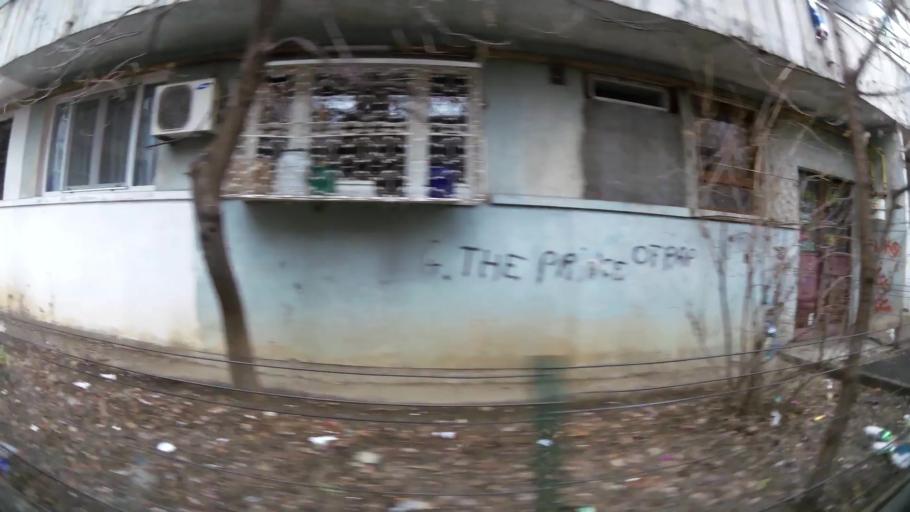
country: RO
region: Ilfov
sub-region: Comuna Chiajna
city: Rosu
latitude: 44.4599
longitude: 26.0474
